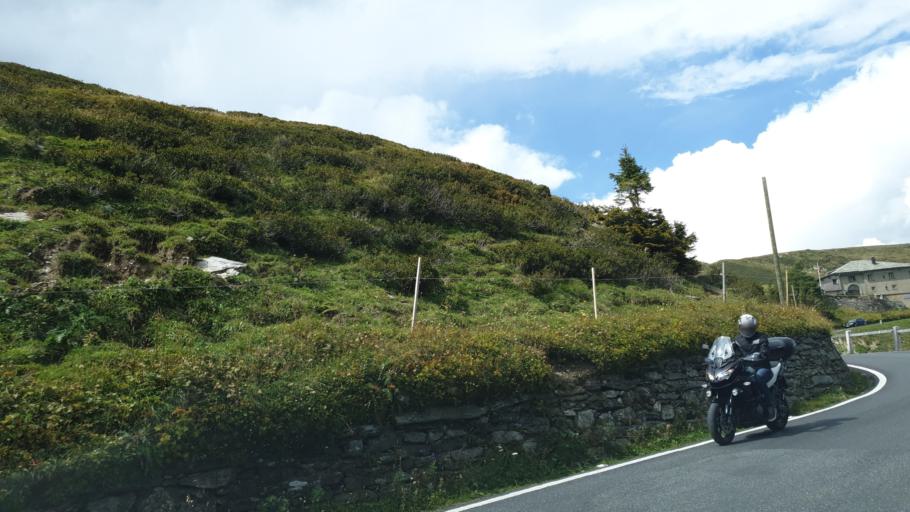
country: IT
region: Lombardy
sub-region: Provincia di Sondrio
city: Campodolcino
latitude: 46.5109
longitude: 9.3289
